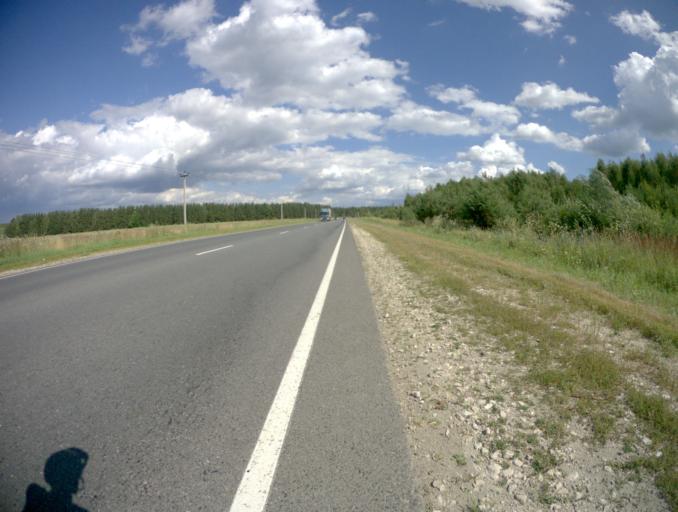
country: RU
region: Vladimir
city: Andreyevo
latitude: 55.9353
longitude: 41.0897
